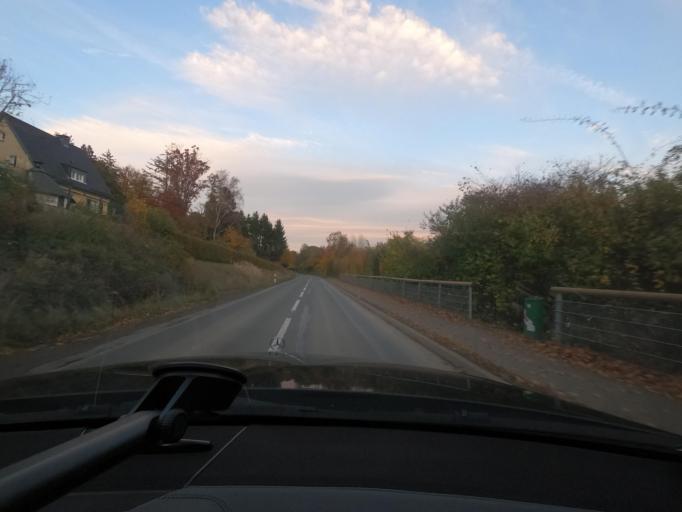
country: DE
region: North Rhine-Westphalia
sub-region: Regierungsbezirk Arnsberg
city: Mohnesee
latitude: 51.4928
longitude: 8.1410
